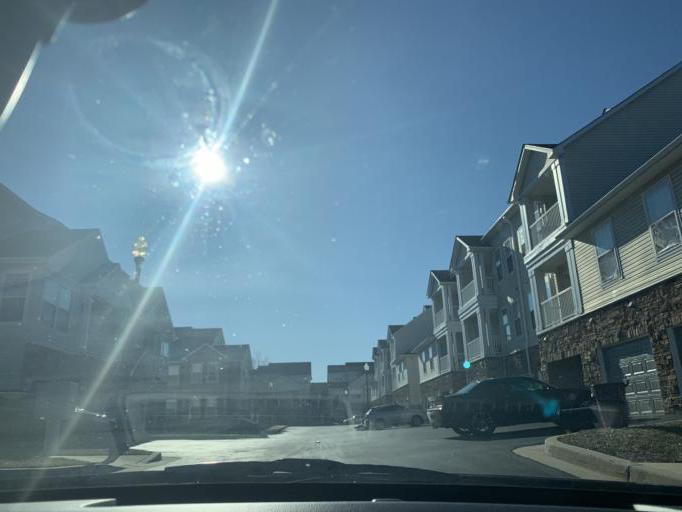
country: US
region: Maryland
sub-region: Baltimore County
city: Garrison
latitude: 39.3984
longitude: -76.7463
